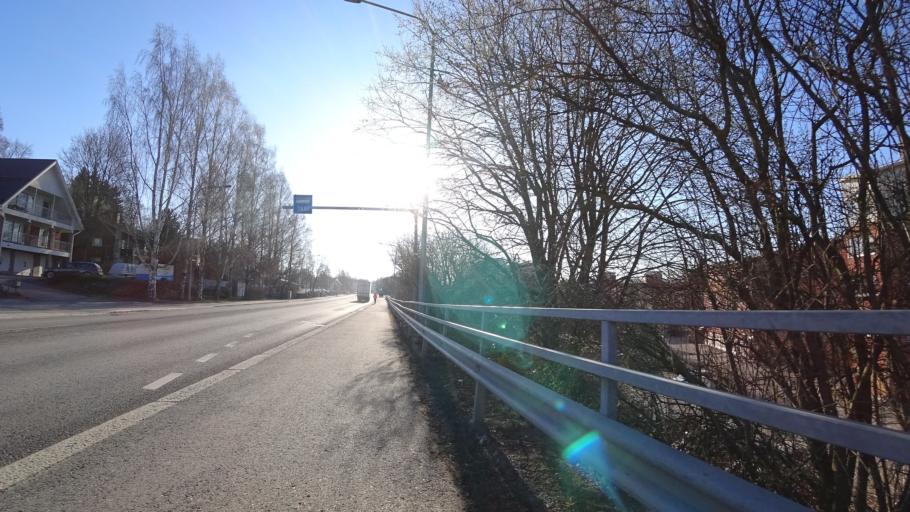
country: FI
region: Pirkanmaa
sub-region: Tampere
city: Pirkkala
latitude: 61.5087
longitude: 23.6798
